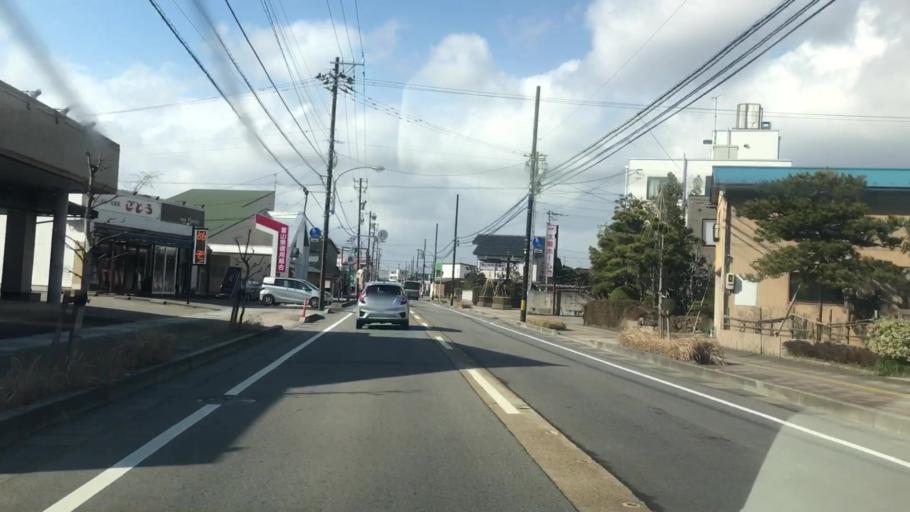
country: JP
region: Toyama
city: Takaoka
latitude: 36.7301
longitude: 137.0563
